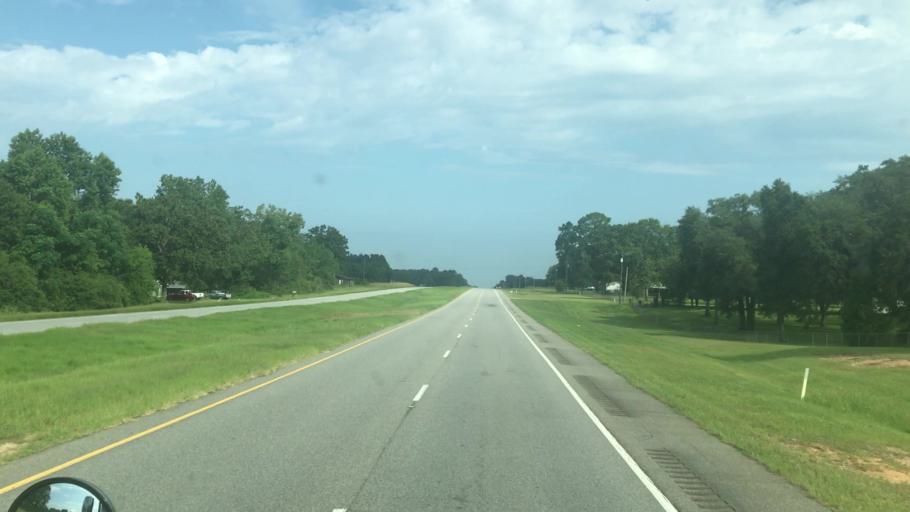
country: US
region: Georgia
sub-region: Early County
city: Blakely
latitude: 31.3107
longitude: -84.8712
